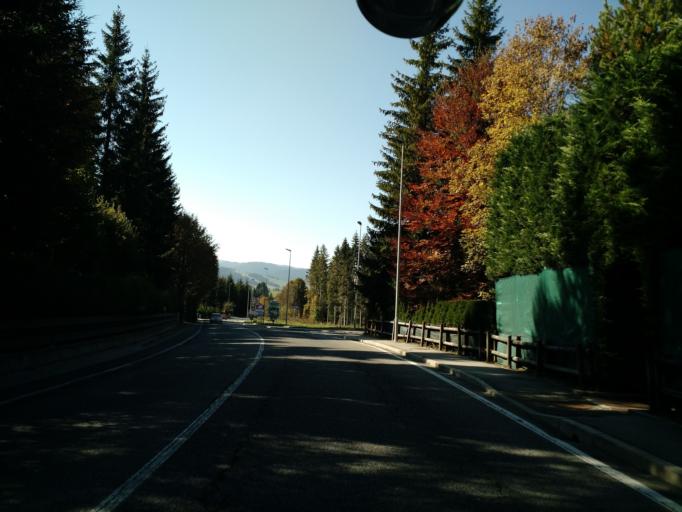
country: IT
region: Veneto
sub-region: Provincia di Vicenza
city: Gallio
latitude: 45.8836
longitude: 11.5341
